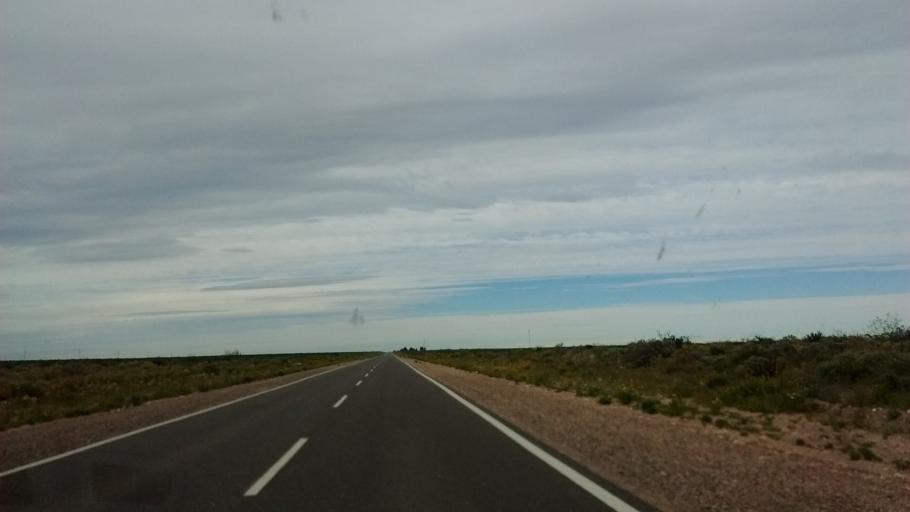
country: AR
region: Rio Negro
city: Contraalmirante Cordero
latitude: -38.3776
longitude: -68.0228
